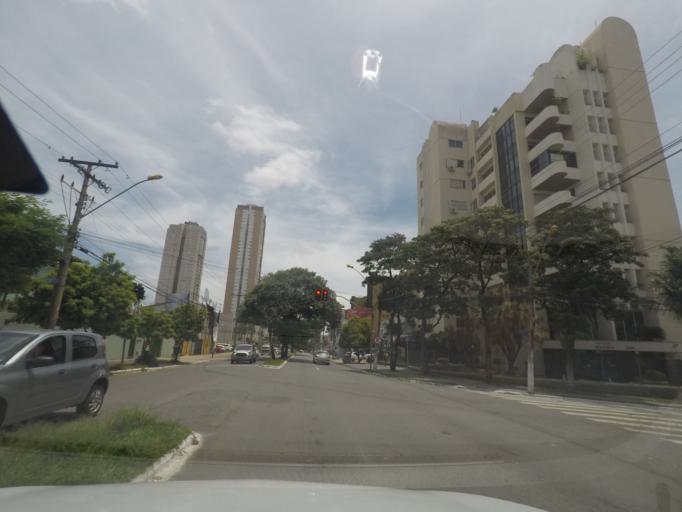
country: BR
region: Goias
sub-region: Goiania
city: Goiania
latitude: -16.6912
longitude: -49.2644
